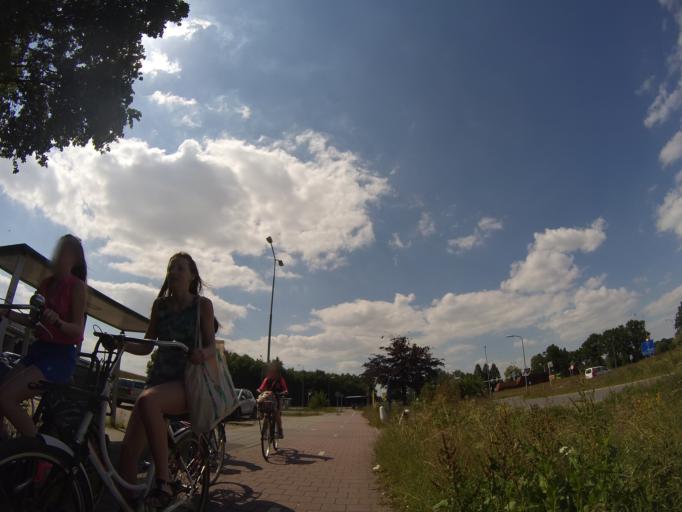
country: NL
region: Gelderland
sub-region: Gemeente Barneveld
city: Voorthuizen
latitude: 52.1694
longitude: 5.5981
